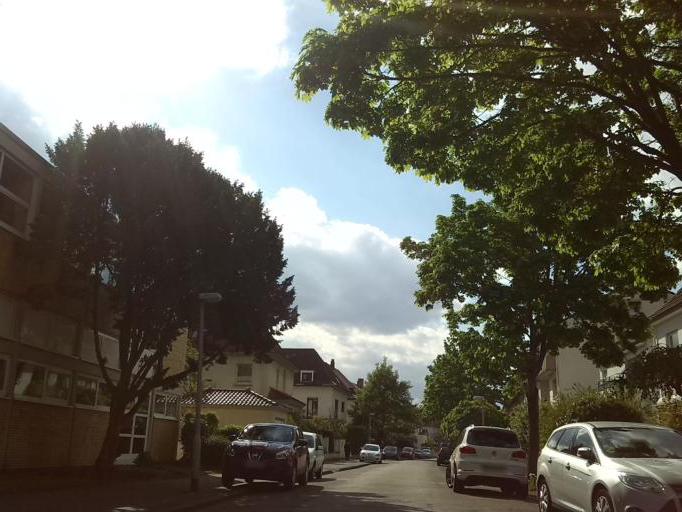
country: DE
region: Baden-Wuerttemberg
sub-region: Karlsruhe Region
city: Mannheim
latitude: 49.4907
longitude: 8.5238
